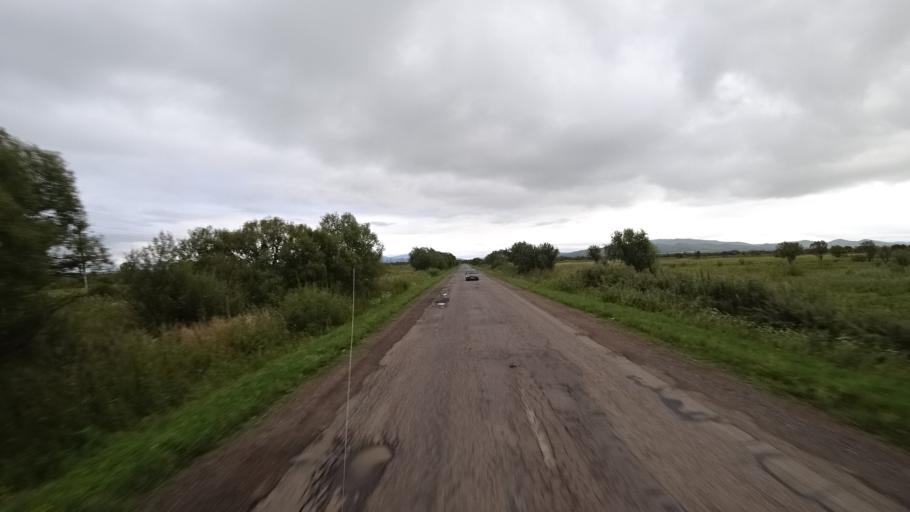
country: RU
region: Primorskiy
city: Chernigovka
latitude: 44.3610
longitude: 132.5553
